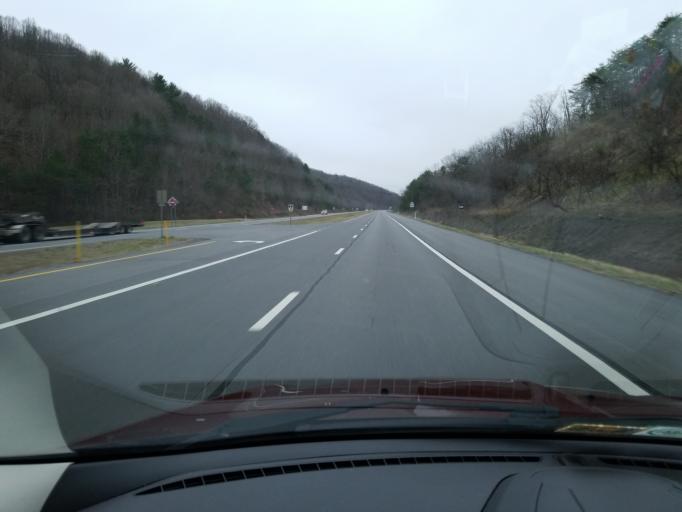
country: US
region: West Virginia
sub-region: Mercer County
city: Athens
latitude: 37.3428
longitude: -80.9579
